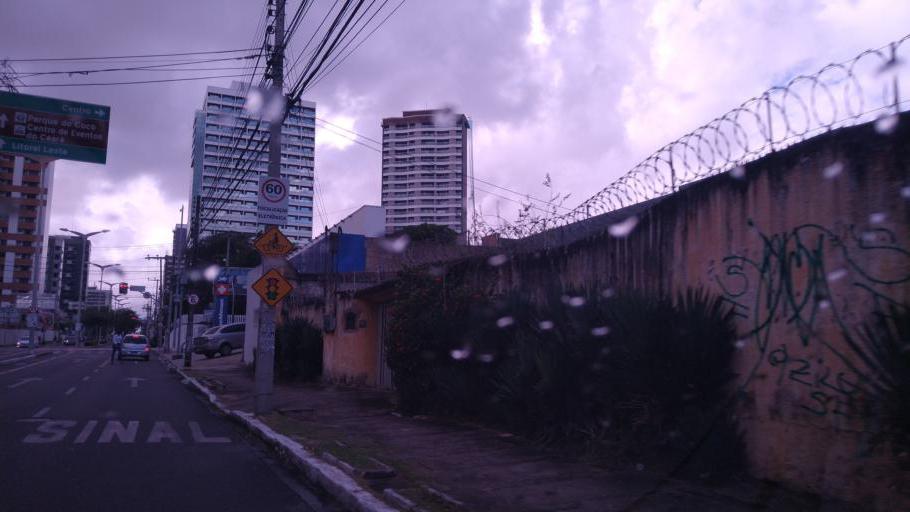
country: BR
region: Ceara
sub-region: Fortaleza
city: Fortaleza
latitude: -3.7372
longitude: -38.4934
